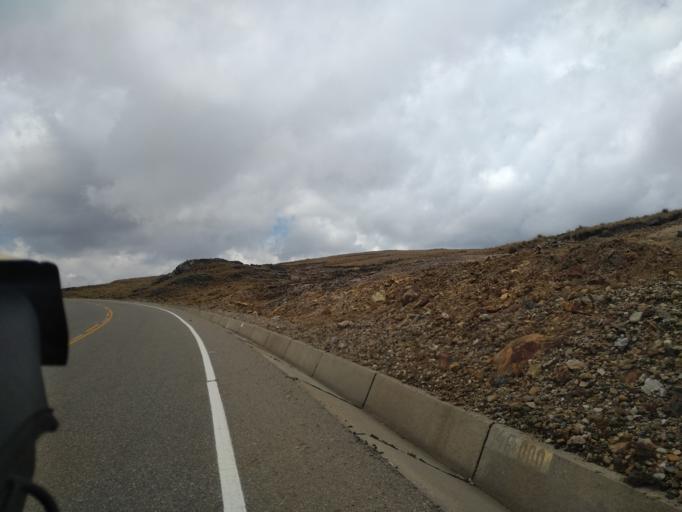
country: PE
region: La Libertad
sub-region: Provincia de Santiago de Chuco
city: Quiruvilca
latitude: -7.9626
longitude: -78.1976
